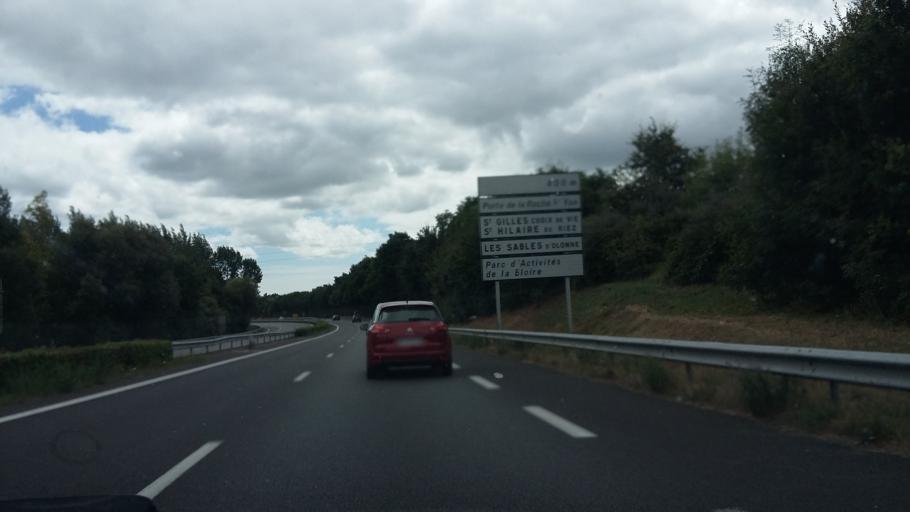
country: FR
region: Pays de la Loire
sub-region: Departement de la Vendee
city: Challans
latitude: 46.8457
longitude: -1.8523
